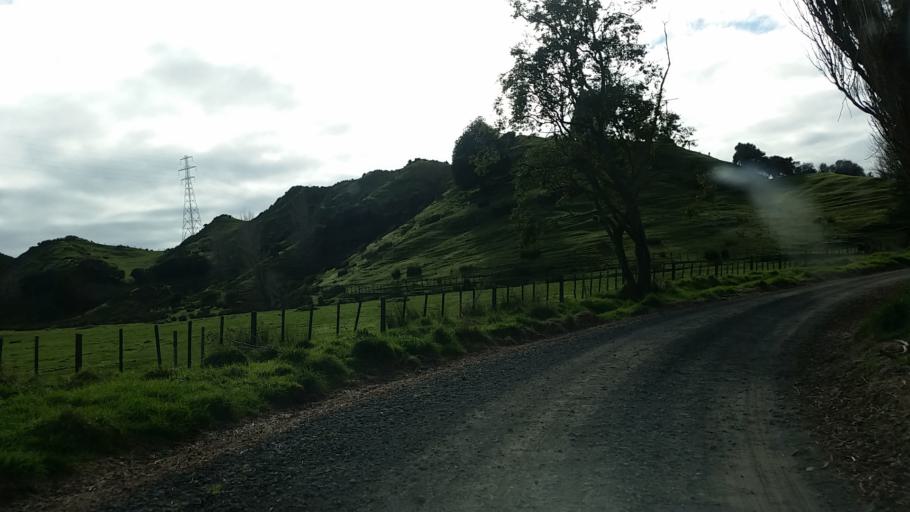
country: NZ
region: Taranaki
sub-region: South Taranaki District
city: Eltham
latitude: -39.2546
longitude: 174.5294
